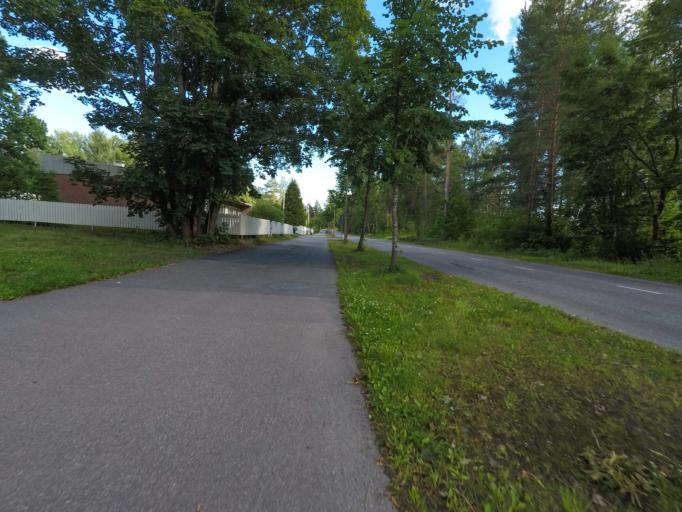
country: FI
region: South Karelia
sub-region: Lappeenranta
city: Lappeenranta
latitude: 61.0692
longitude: 28.1555
